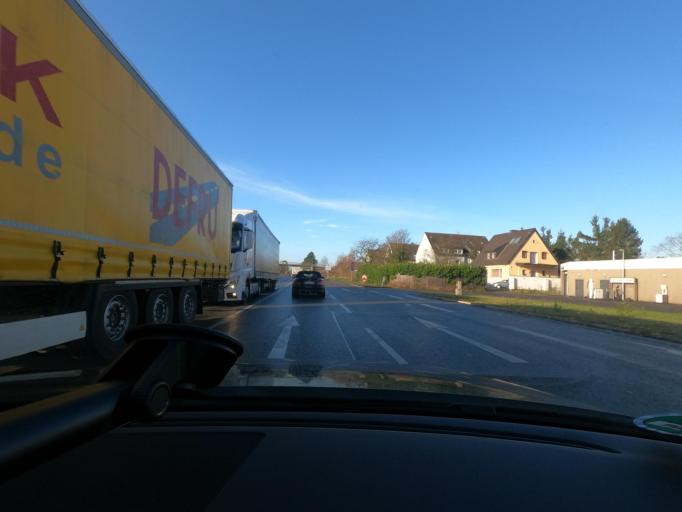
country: DE
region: North Rhine-Westphalia
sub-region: Regierungsbezirk Dusseldorf
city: Hochfeld
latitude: 51.3584
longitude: 6.6877
